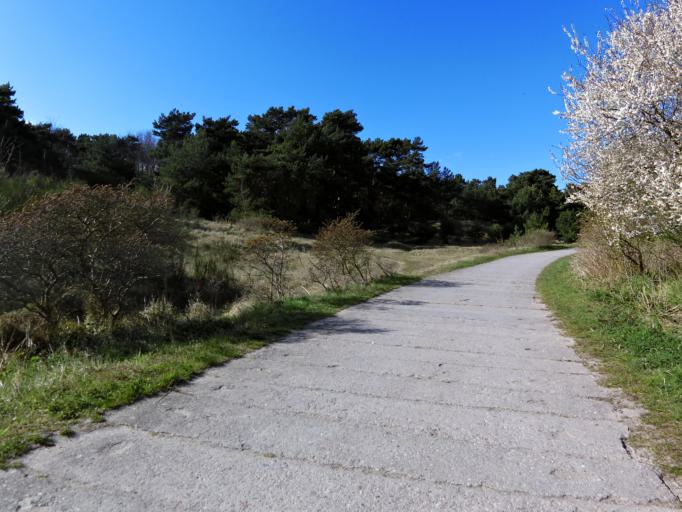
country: DE
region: Mecklenburg-Vorpommern
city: Hiddensee
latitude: 54.5923
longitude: 13.1109
